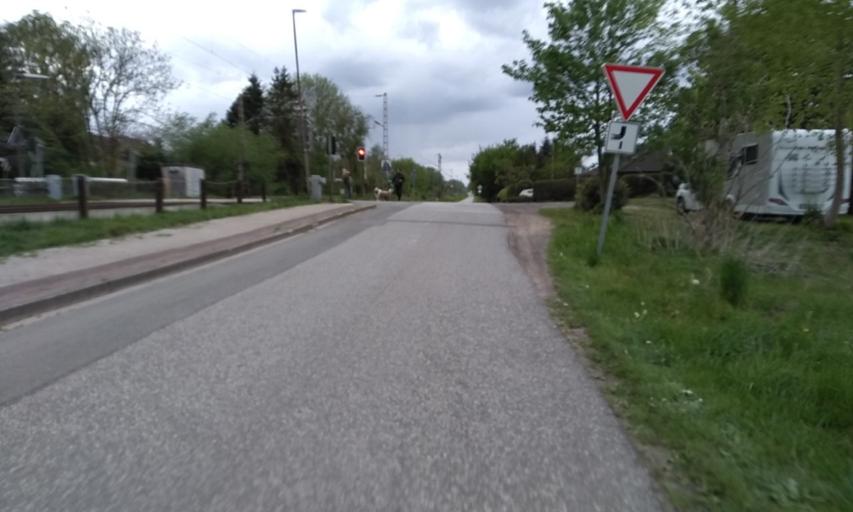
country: DE
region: Lower Saxony
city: Nottensdorf
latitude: 53.4844
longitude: 9.6322
